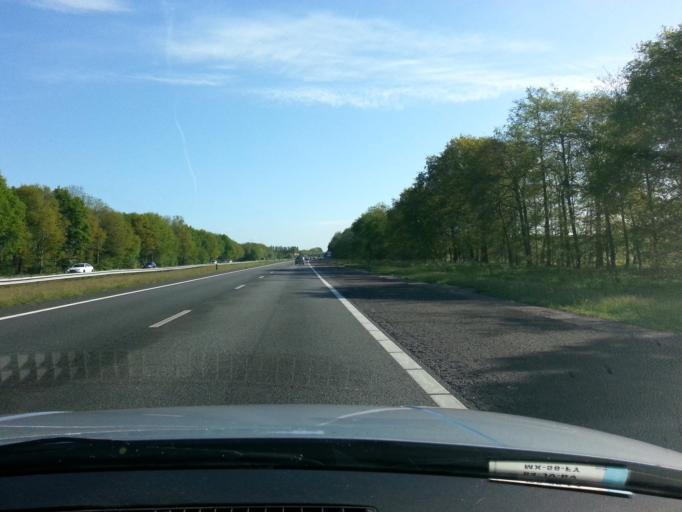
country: NL
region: North Holland
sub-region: Gemeente Blaricum
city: Blaricum
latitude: 52.2734
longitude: 5.2620
